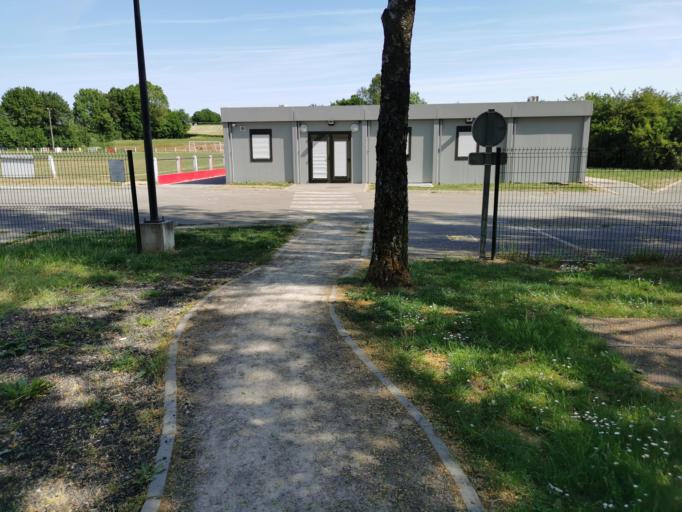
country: FR
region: Nord-Pas-de-Calais
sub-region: Departement du Nord
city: Marpent
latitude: 50.1787
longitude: 4.0897
